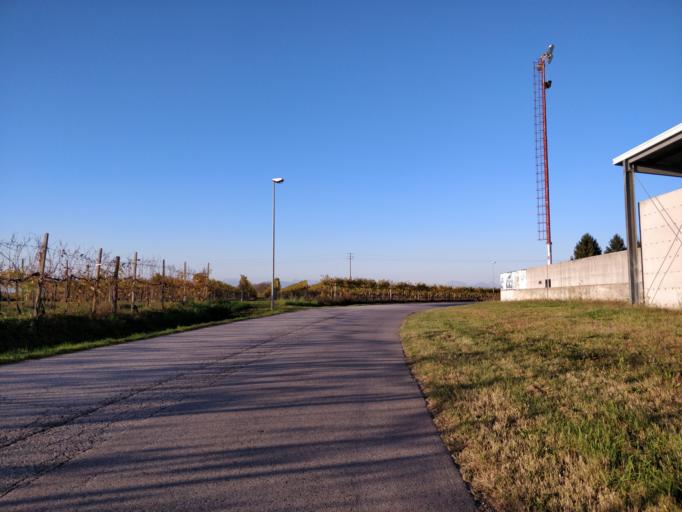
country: IT
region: Friuli Venezia Giulia
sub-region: Provincia di Udine
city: Bertiolo
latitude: 45.9494
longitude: 13.0455
